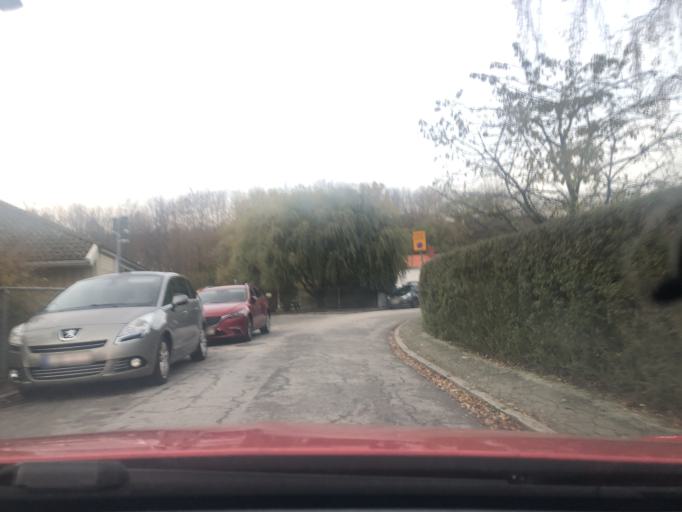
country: SE
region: Skane
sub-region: Burlovs Kommun
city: Arloev
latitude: 55.6028
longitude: 13.0806
